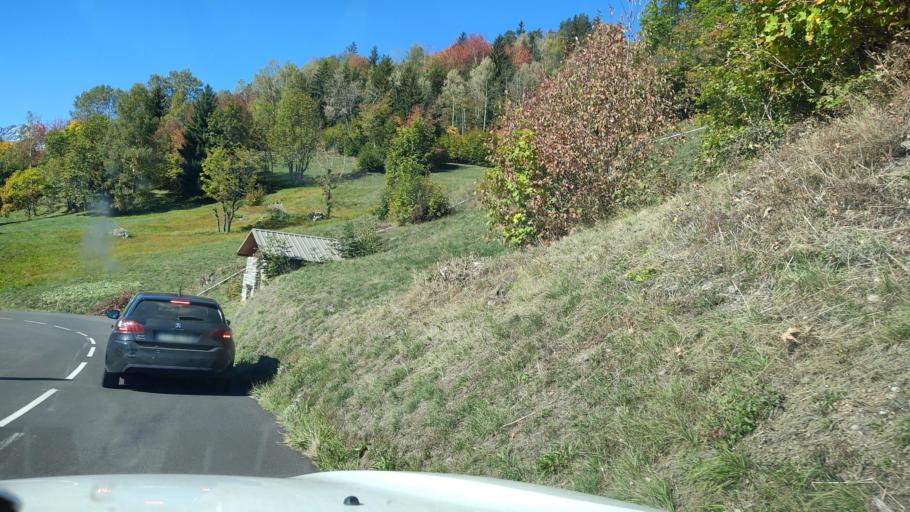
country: FR
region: Rhone-Alpes
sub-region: Departement de la Savoie
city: Seez
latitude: 45.6129
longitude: 6.8584
